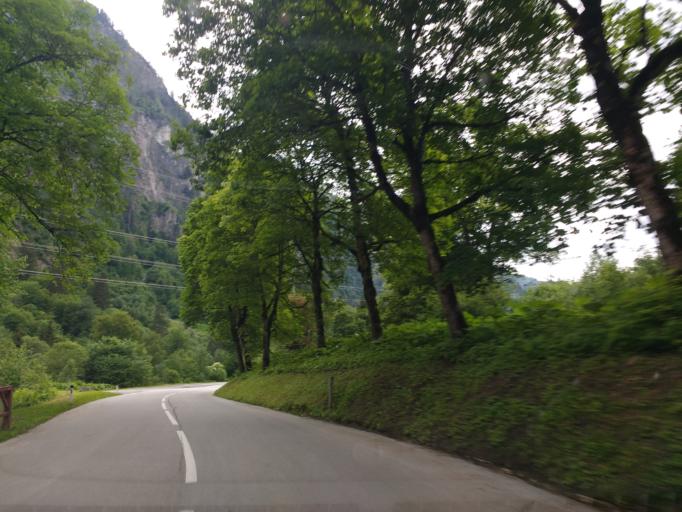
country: AT
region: Salzburg
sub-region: Politischer Bezirk Zell am See
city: Kaprun
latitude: 47.2223
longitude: 12.7278
